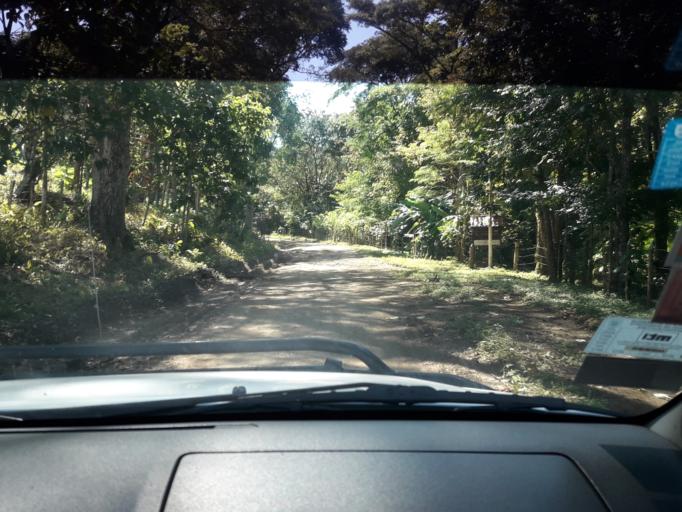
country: CR
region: Guanacaste
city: La Cruz
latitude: 11.2003
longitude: -85.6572
